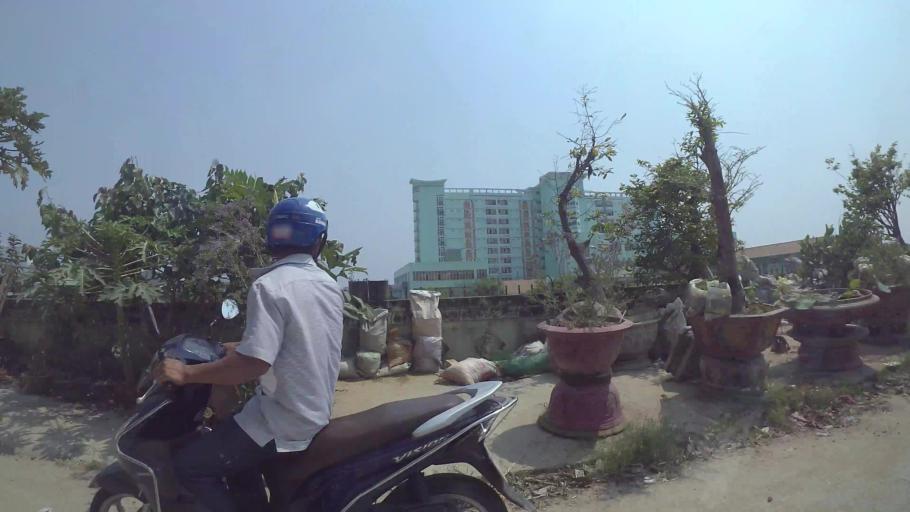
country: VN
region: Da Nang
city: Ngu Hanh Son
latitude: 16.0229
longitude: 108.2479
